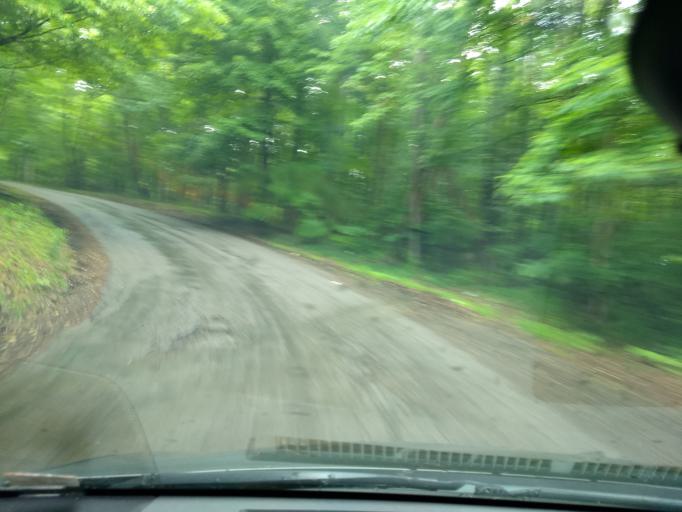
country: US
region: Pennsylvania
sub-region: Armstrong County
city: Orchard Hills
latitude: 40.5556
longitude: -79.5072
